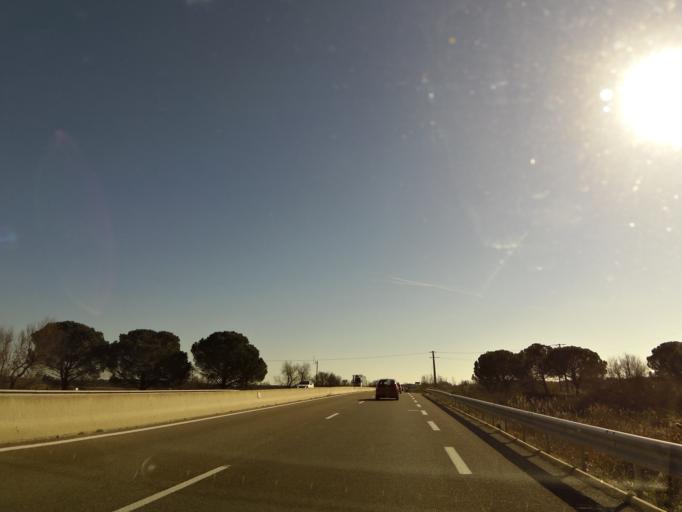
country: FR
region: Languedoc-Roussillon
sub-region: Departement du Gard
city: Aigues-Mortes
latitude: 43.5973
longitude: 4.1954
